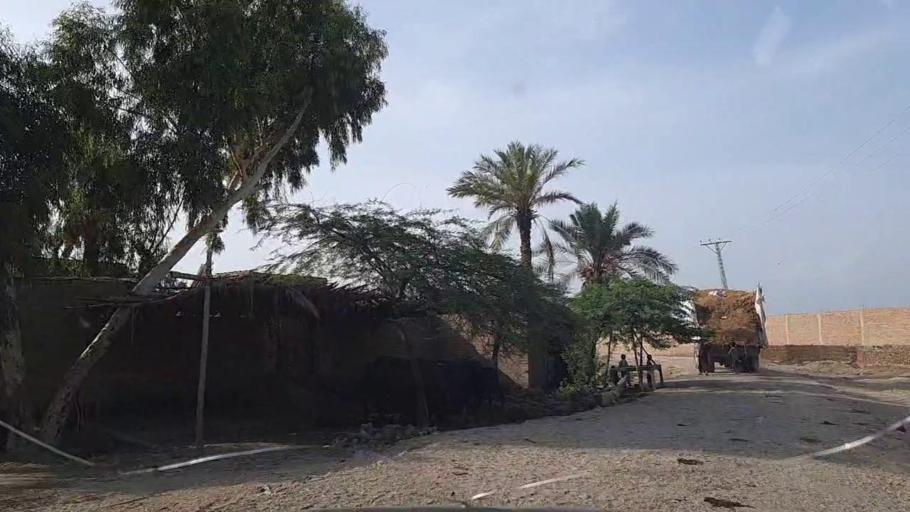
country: PK
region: Sindh
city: Ghotki
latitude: 28.0104
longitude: 69.2950
